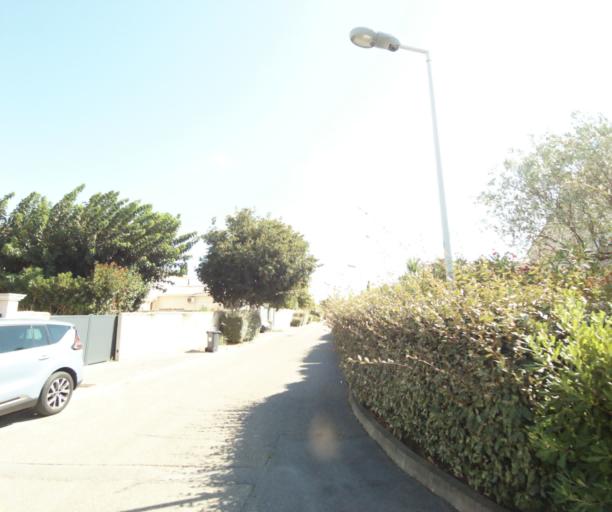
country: FR
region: Languedoc-Roussillon
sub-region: Departement du Gard
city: Bouillargues
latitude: 43.8041
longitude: 4.4345
